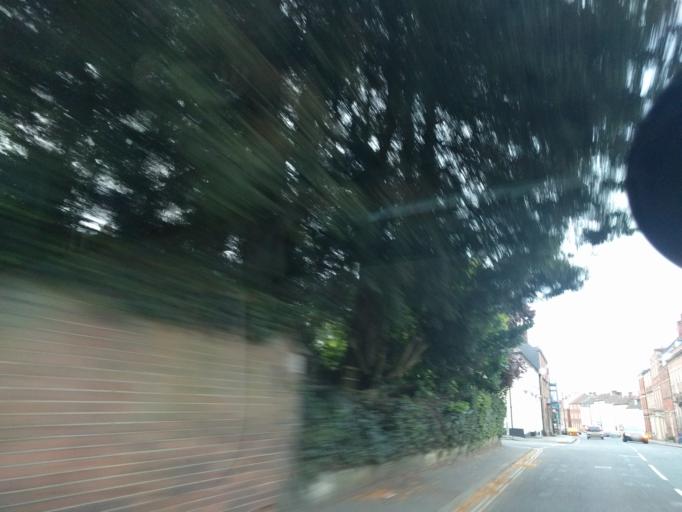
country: GB
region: England
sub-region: Wiltshire
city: Devizes
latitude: 51.3485
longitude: -1.9925
